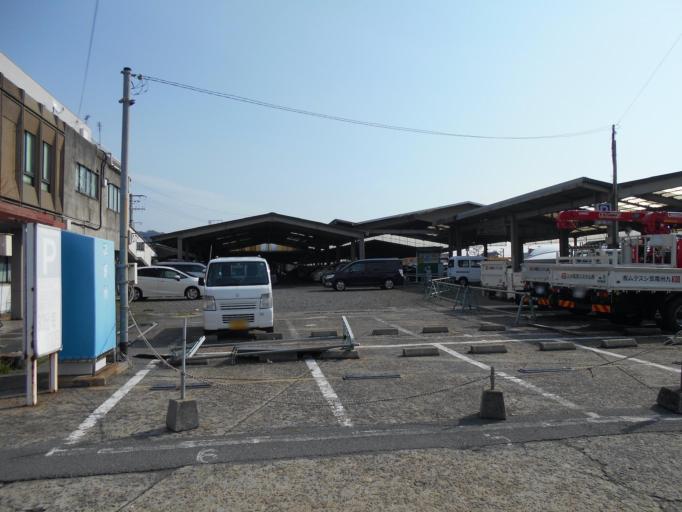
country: JP
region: Kagoshima
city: Kagoshima-shi
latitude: 31.6012
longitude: 130.5630
